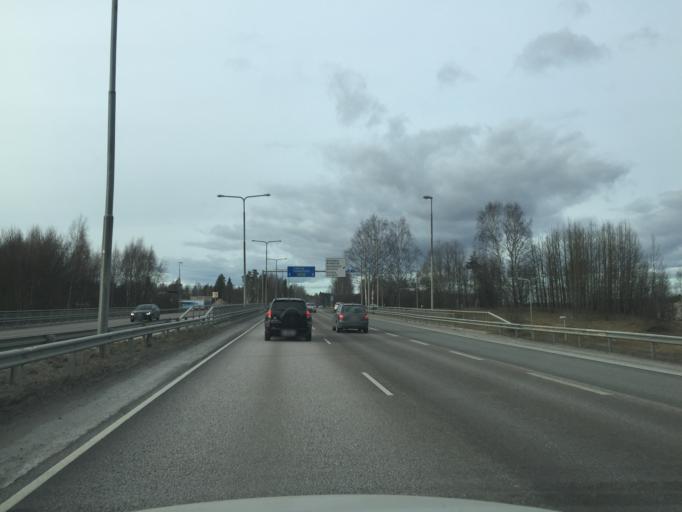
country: FI
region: Uusimaa
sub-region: Helsinki
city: Teekkarikylae
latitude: 60.2620
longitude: 24.8764
